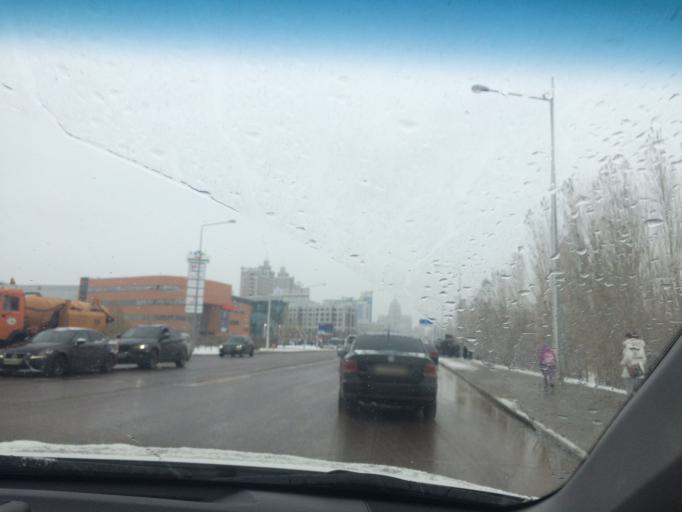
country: KZ
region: Astana Qalasy
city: Astana
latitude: 51.1259
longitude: 71.4132
